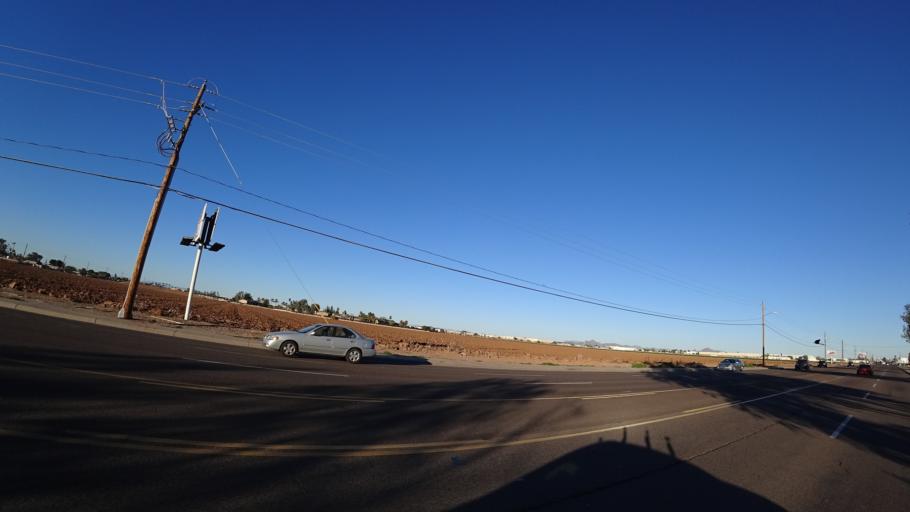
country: US
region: Arizona
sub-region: Maricopa County
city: Tolleson
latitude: 33.4514
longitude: -112.1848
